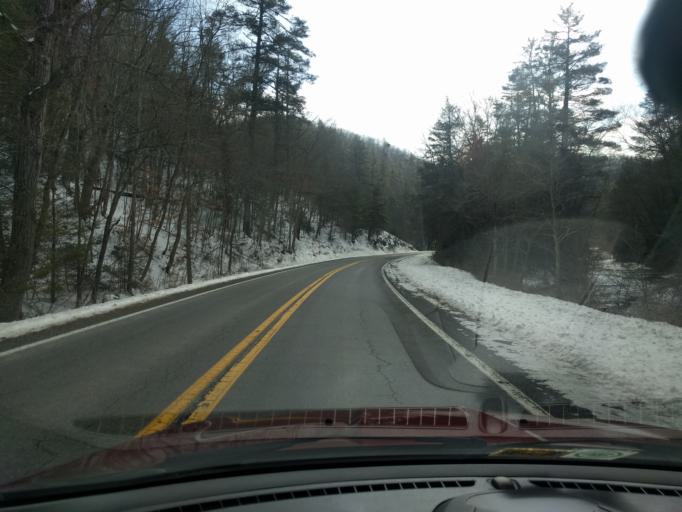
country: US
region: West Virginia
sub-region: Pocahontas County
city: Marlinton
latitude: 38.1372
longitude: -79.9633
